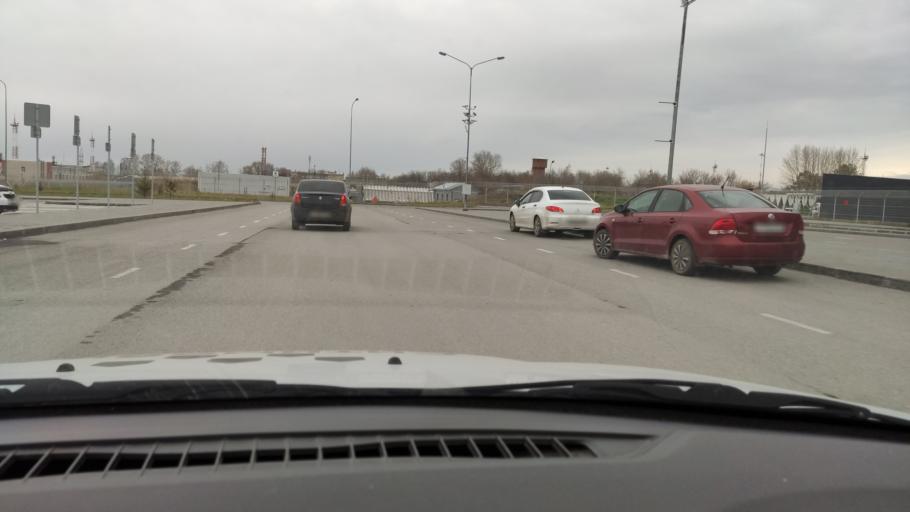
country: RU
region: Perm
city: Kultayevo
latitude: 57.9168
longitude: 56.0096
